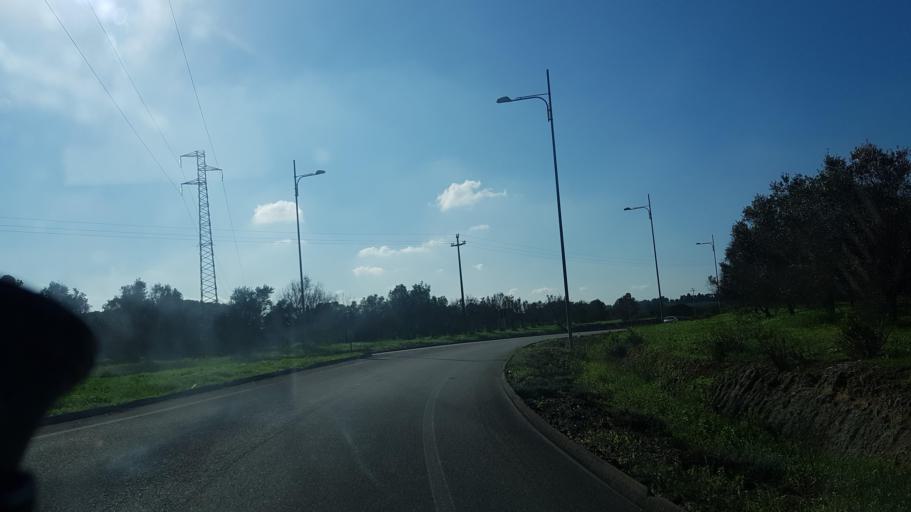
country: IT
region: Apulia
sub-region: Provincia di Lecce
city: San Pietro in Lama
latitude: 40.3359
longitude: 18.1369
